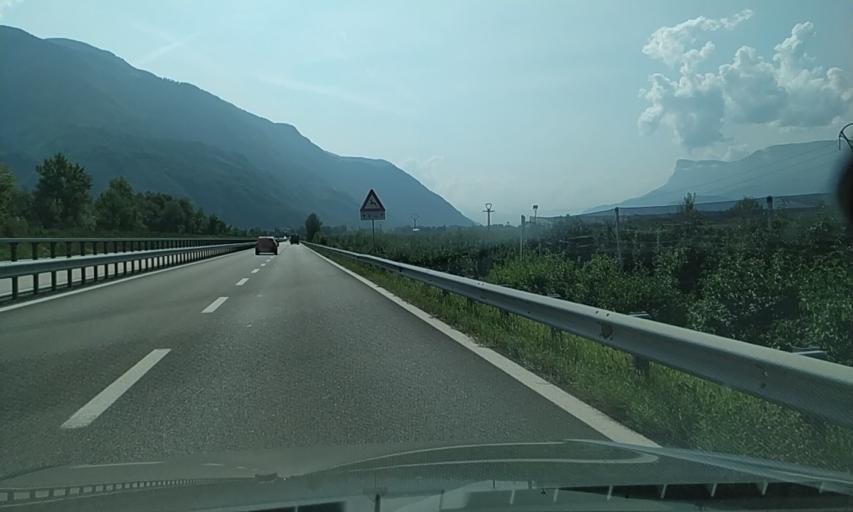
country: IT
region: Trentino-Alto Adige
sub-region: Bolzano
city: Marlengo
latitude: 46.6446
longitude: 11.1617
